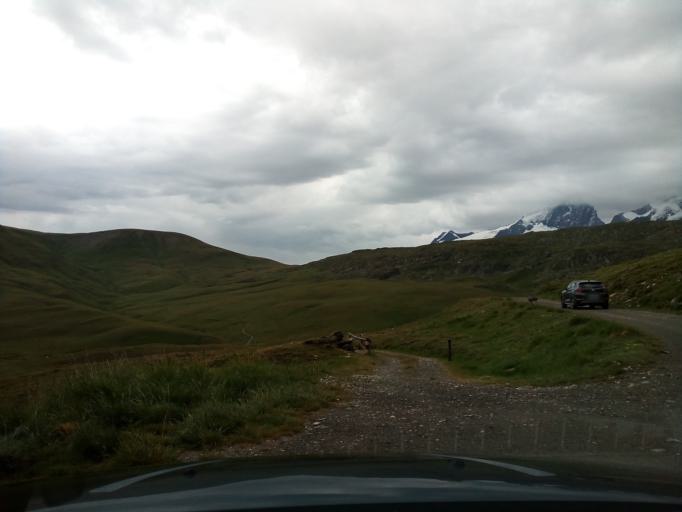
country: FR
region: Rhone-Alpes
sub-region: Departement de l'Isere
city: Mont-de-Lans
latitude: 45.0668
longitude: 6.2117
